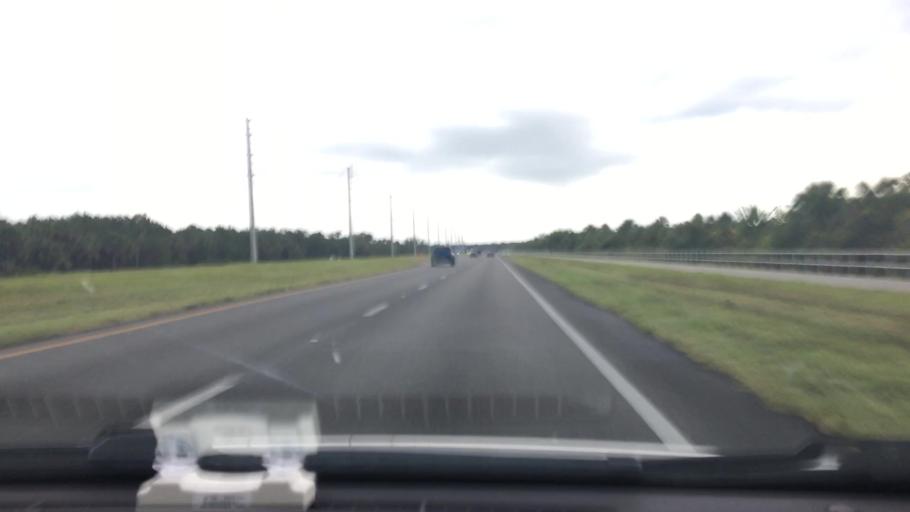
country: US
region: Florida
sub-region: Seminole County
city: Midway
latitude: 28.8098
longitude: -81.2008
